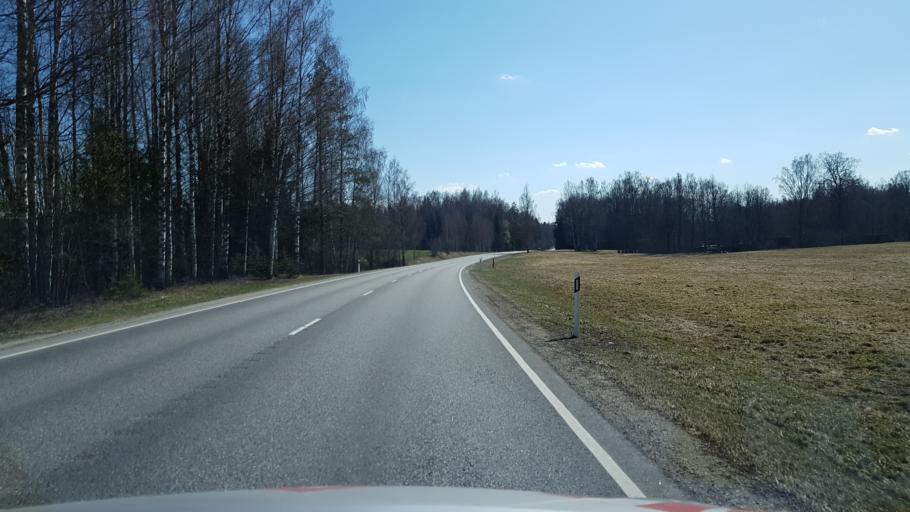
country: EE
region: Jogevamaa
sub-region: Mustvee linn
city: Mustvee
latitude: 58.6989
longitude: 26.8171
